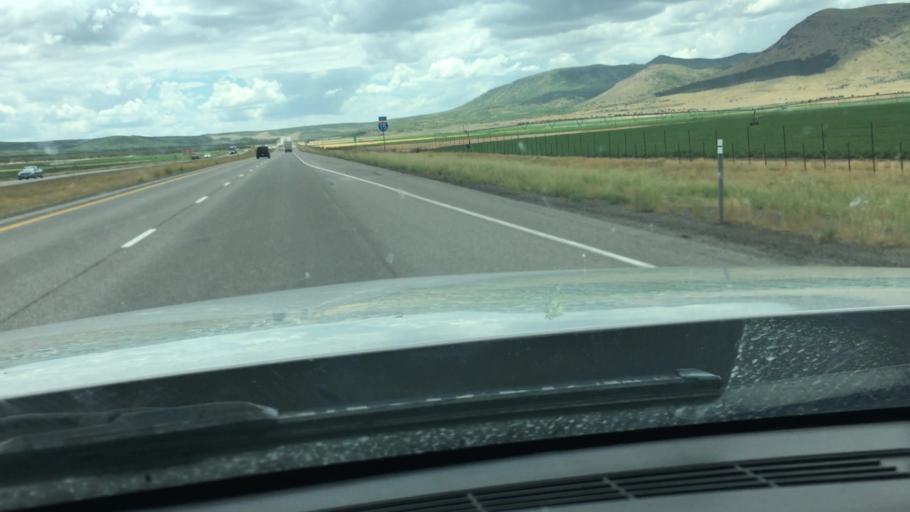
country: US
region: Utah
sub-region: Beaver County
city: Beaver
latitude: 38.5326
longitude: -112.6107
